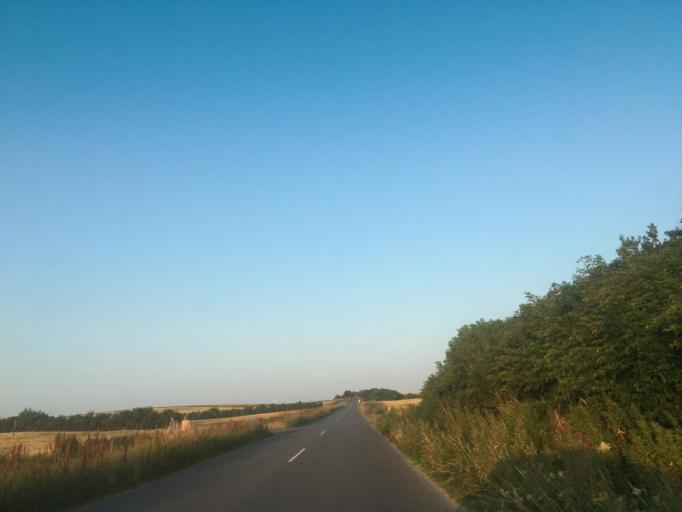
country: DK
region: North Denmark
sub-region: Thisted Kommune
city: Hurup
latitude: 56.7616
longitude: 8.3326
